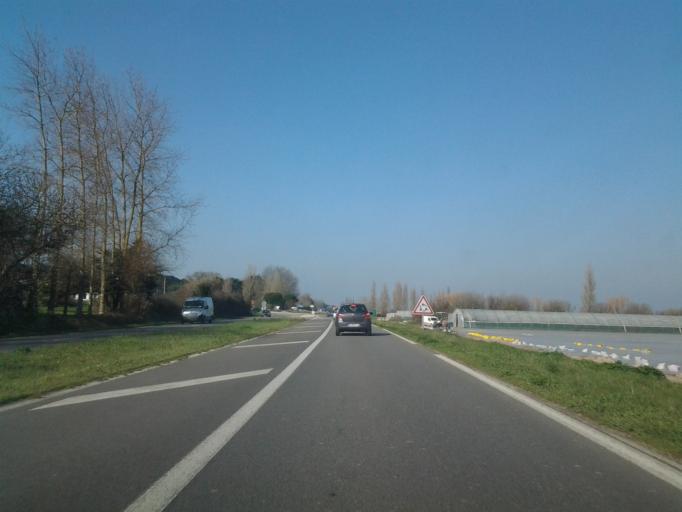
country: FR
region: Pays de la Loire
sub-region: Departement de la Vendee
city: Barbatre
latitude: 46.9607
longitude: -2.2017
